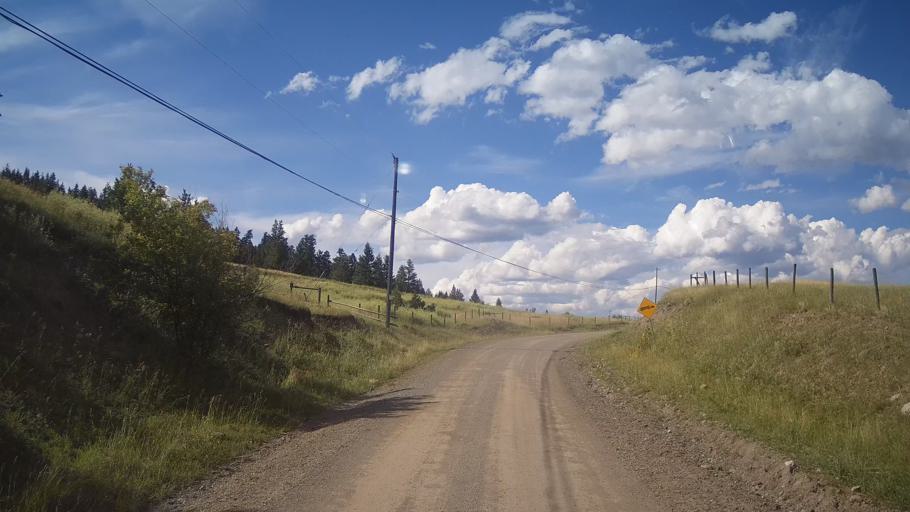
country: CA
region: British Columbia
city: Lillooet
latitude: 51.3063
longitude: -121.9875
